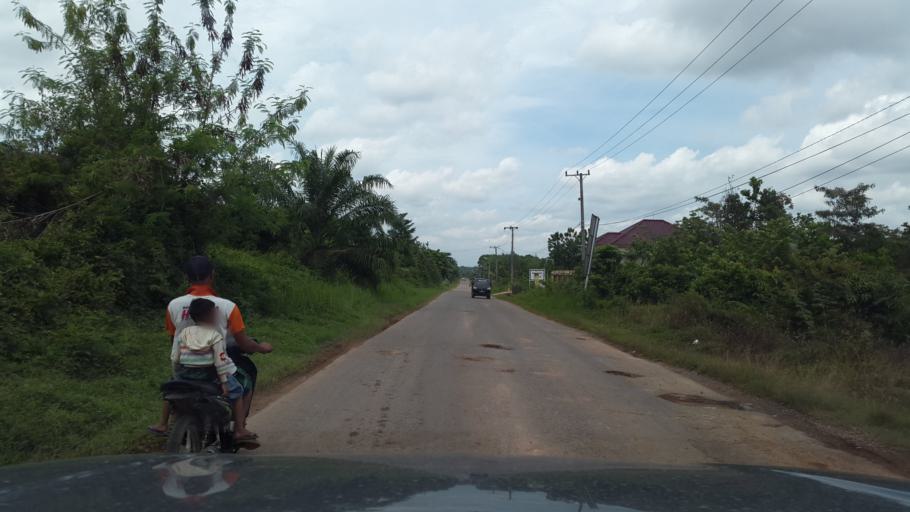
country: ID
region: South Sumatra
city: Gunungmegang Dalam
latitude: -3.3283
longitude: 103.9057
